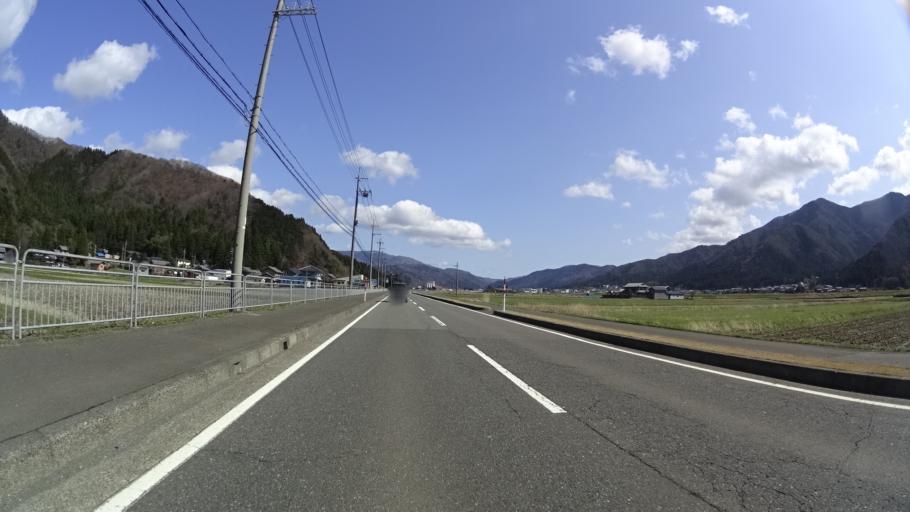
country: JP
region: Fukui
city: Obama
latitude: 35.4724
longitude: 135.8392
